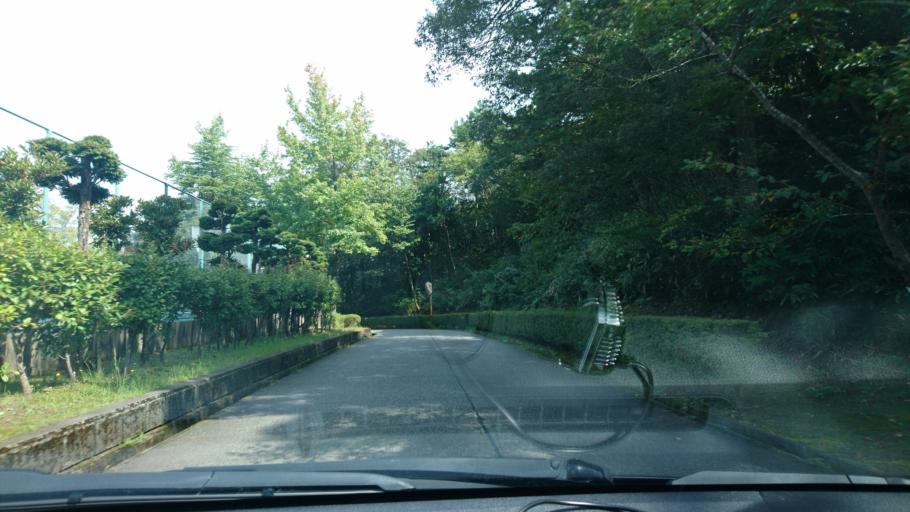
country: JP
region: Ishikawa
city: Komatsu
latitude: 36.3241
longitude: 136.3314
